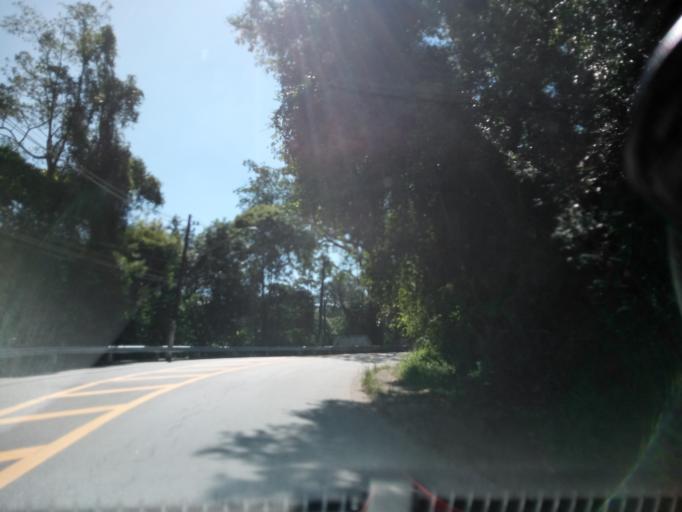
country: BR
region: Sao Paulo
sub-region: Sao Bernardo Do Campo
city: Sao Bernardo do Campo
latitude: -23.7898
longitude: -46.5379
